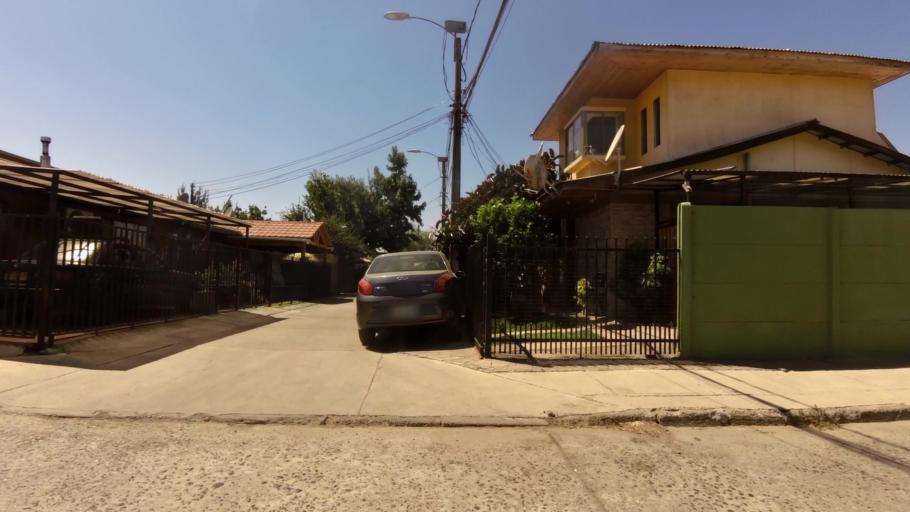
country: CL
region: Maule
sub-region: Provincia de Curico
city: Curico
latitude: -34.9818
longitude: -71.2152
